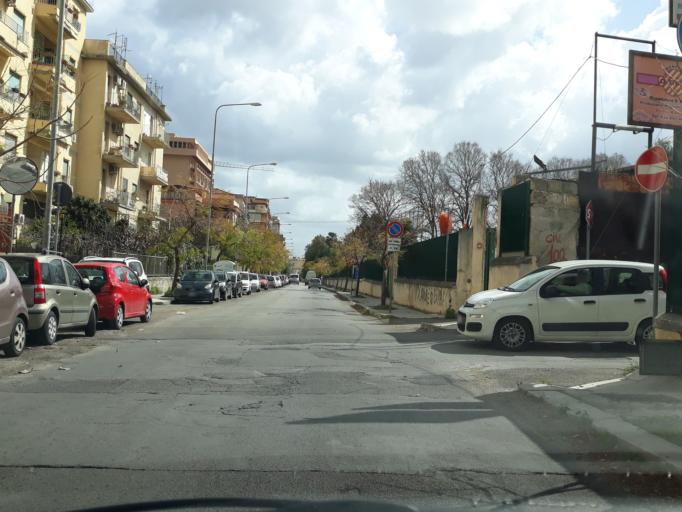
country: IT
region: Sicily
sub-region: Palermo
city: Palermo
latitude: 38.1231
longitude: 13.3217
